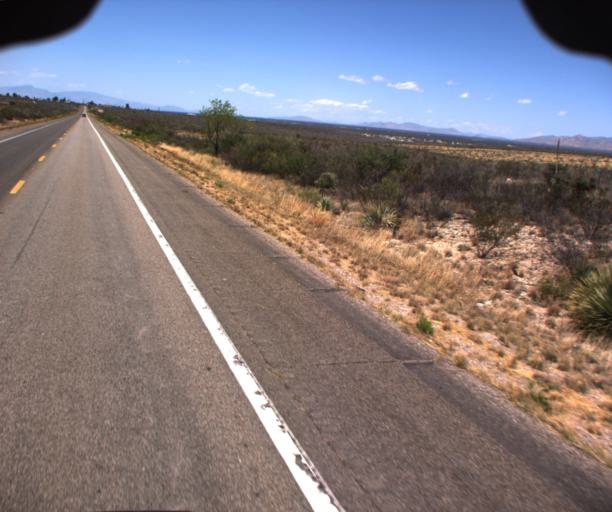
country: US
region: Arizona
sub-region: Cochise County
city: Tombstone
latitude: 31.6955
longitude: -110.0427
